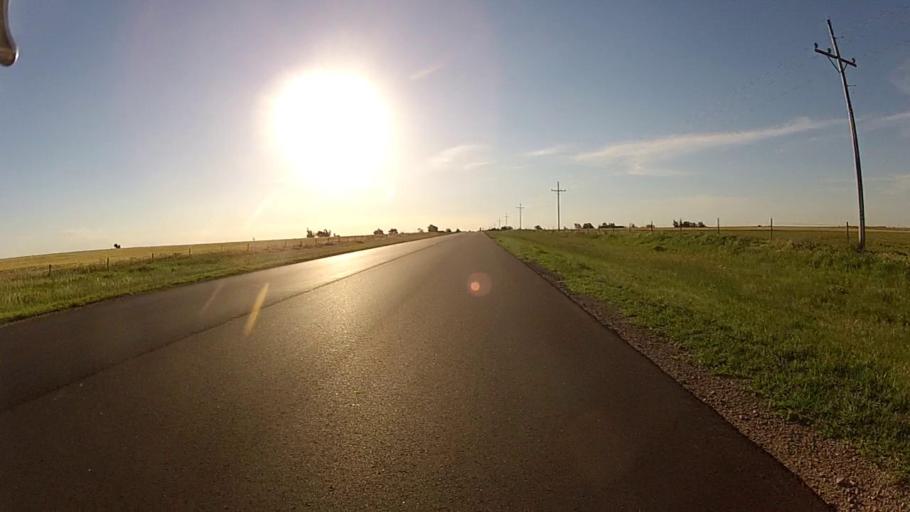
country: US
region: Kansas
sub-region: Comanche County
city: Coldwater
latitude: 37.2815
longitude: -99.1791
